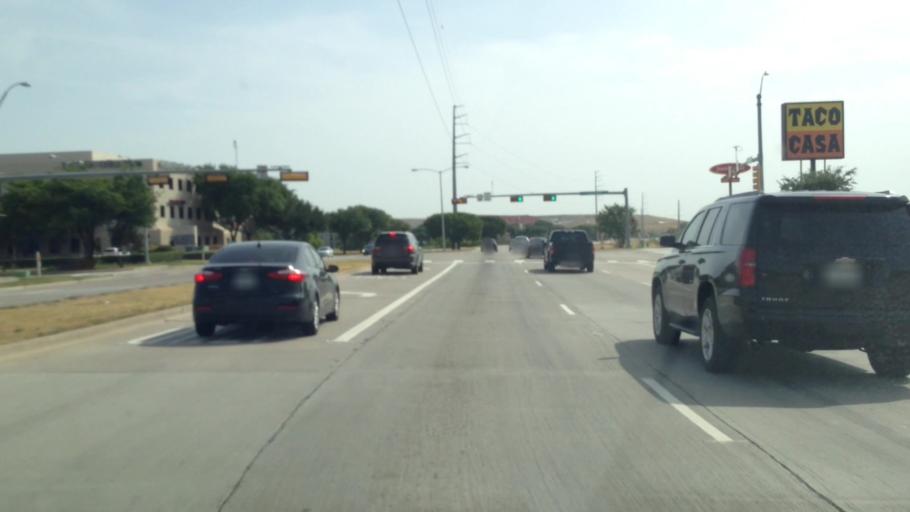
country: US
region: Texas
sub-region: Denton County
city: Lewisville
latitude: 33.0103
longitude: -96.9680
